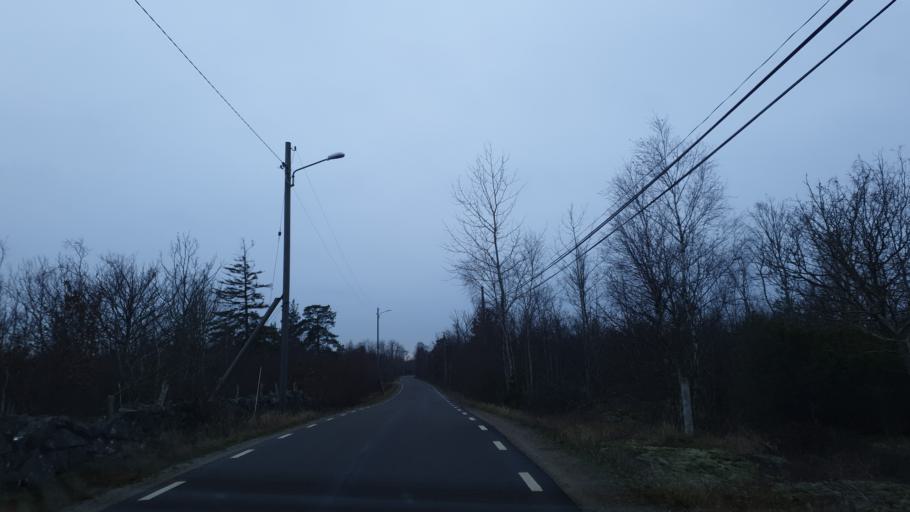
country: SE
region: Blekinge
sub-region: Karlskrona Kommun
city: Karlskrona
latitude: 56.1227
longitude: 15.6246
